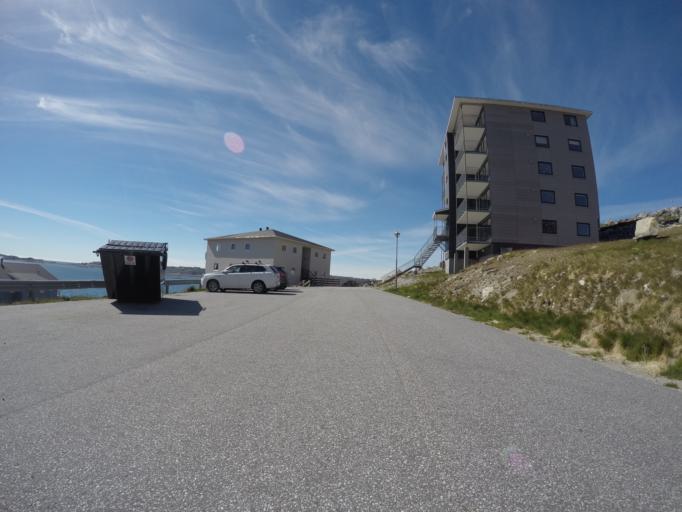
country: GL
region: Sermersooq
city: Nuuk
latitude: 64.1744
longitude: -51.6755
